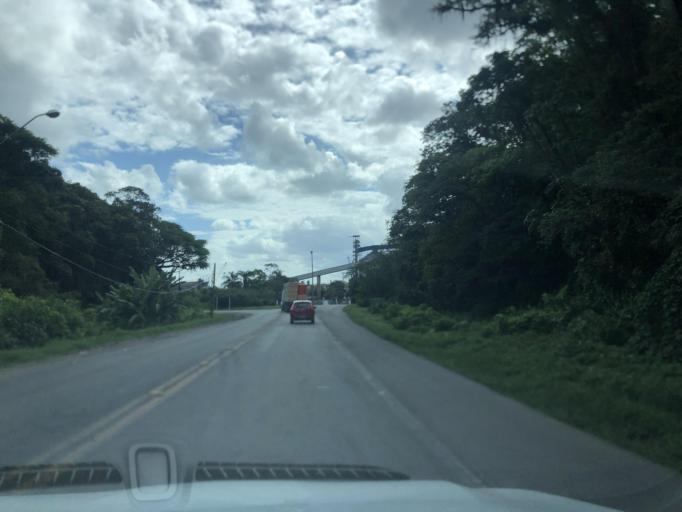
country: BR
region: Santa Catarina
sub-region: Sao Francisco Do Sul
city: Sao Francisco do Sul
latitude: -26.2350
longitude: -48.6280
